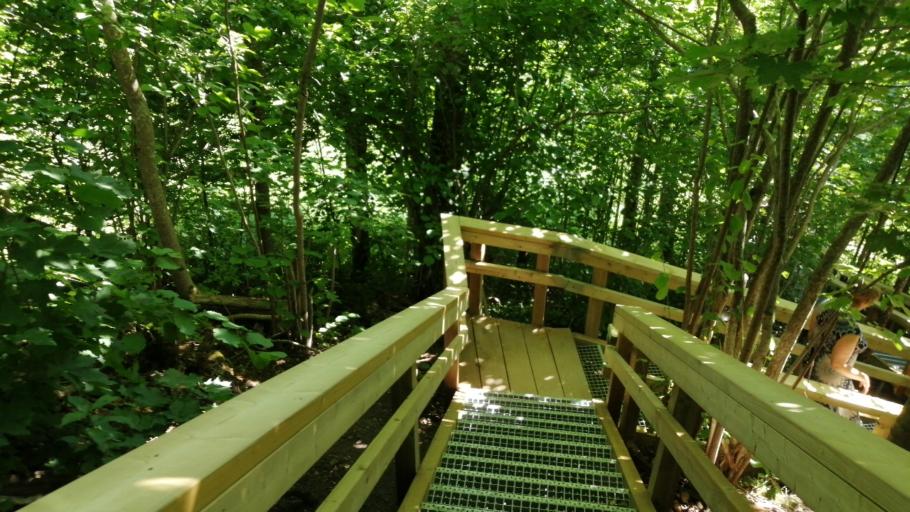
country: EE
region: Vorumaa
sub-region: Voru linn
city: Voru
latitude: 57.7269
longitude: 26.9365
